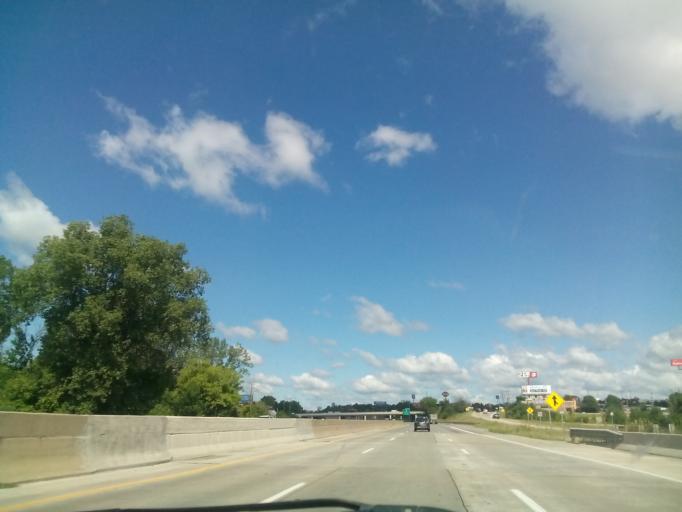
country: US
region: Michigan
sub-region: Genesee County
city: Flint
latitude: 42.9868
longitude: -83.7352
